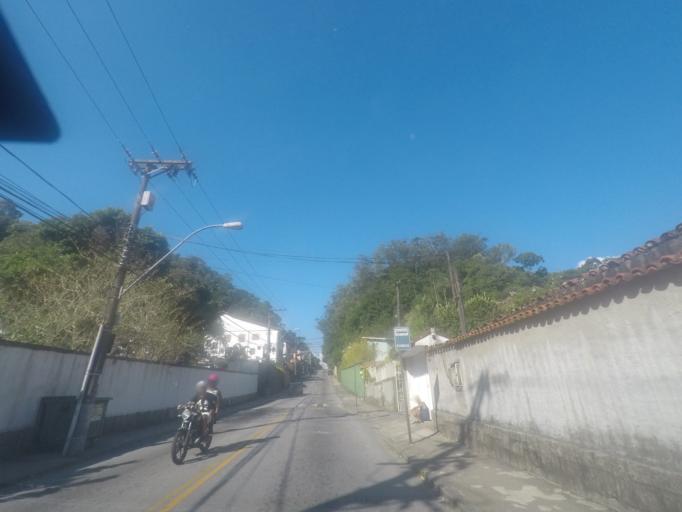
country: BR
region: Rio de Janeiro
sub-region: Petropolis
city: Petropolis
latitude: -22.5320
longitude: -43.1938
